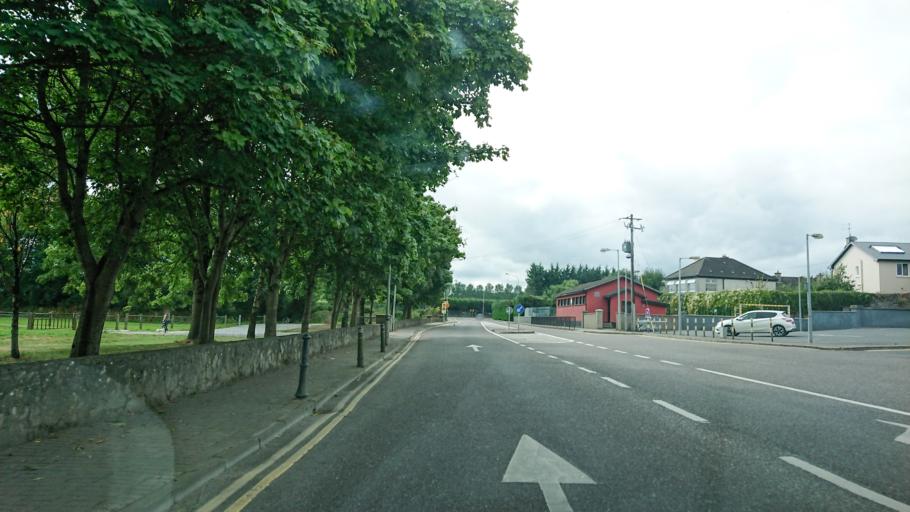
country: IE
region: Munster
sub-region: County Cork
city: Mallow
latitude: 52.1356
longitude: -8.6471
